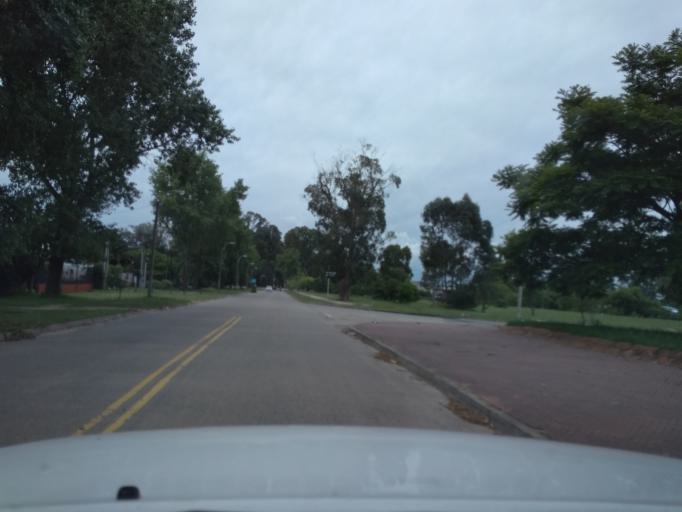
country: UY
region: Canelones
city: Paso de Carrasco
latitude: -34.8692
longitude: -56.0595
